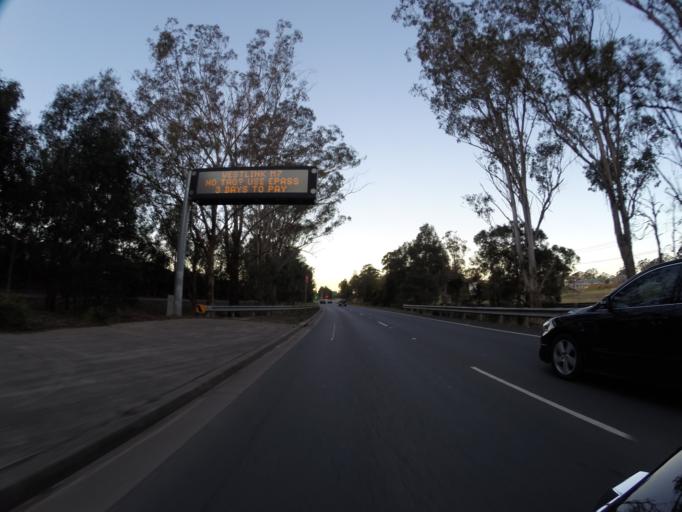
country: AU
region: New South Wales
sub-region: Campbelltown Municipality
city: Glenfield
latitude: -33.9558
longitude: 150.8698
